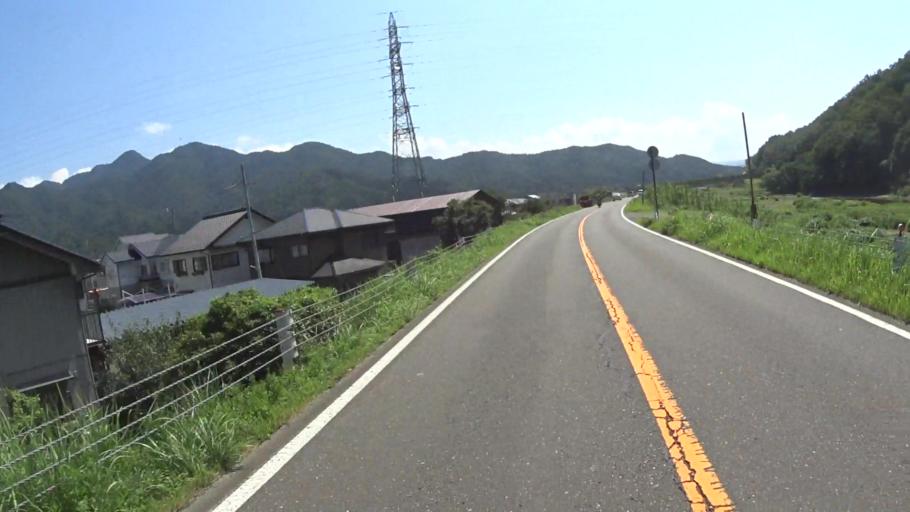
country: JP
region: Fukui
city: Obama
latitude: 35.4834
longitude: 135.7496
